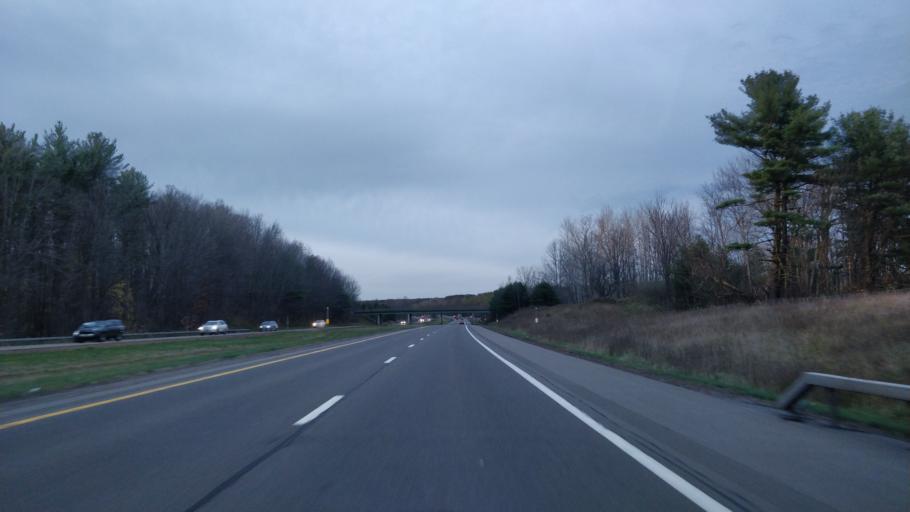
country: US
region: New York
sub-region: Oswego County
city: Central Square
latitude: 43.3245
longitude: -76.1259
